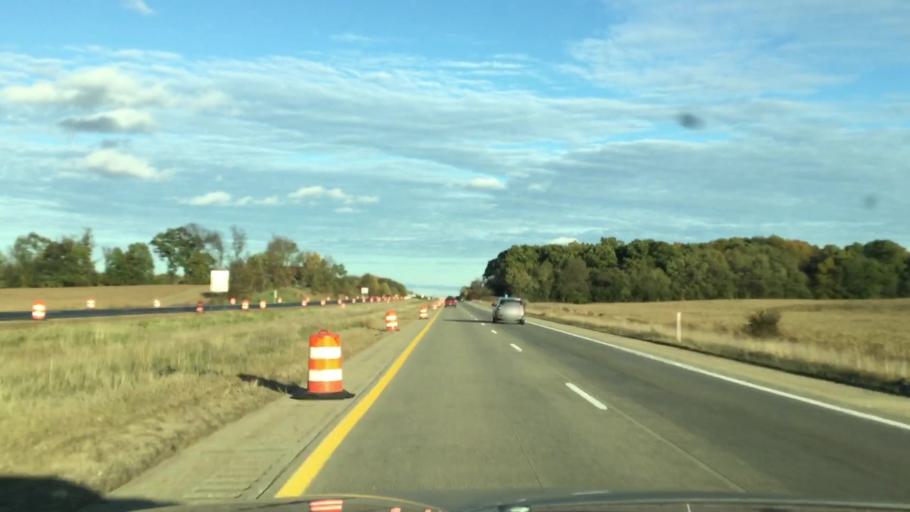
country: US
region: Michigan
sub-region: Calhoun County
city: Marshall
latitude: 42.2827
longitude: -84.8962
